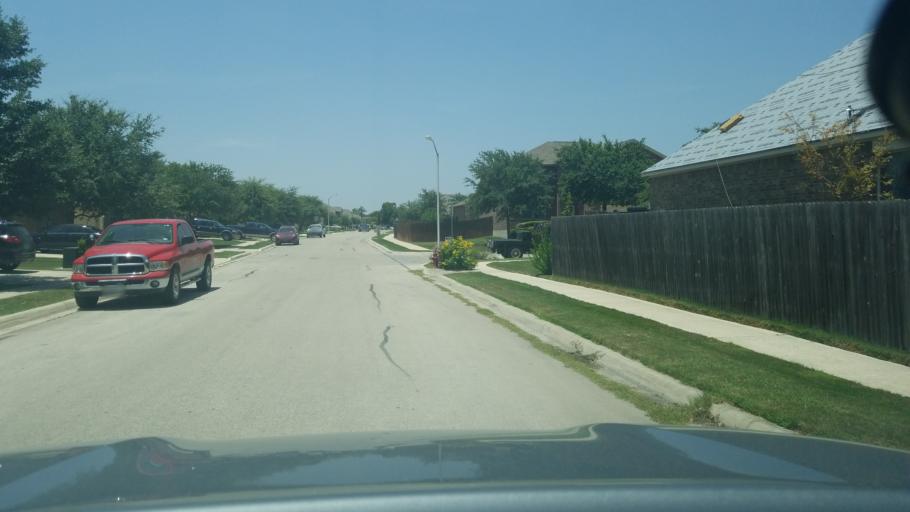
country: US
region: Texas
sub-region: Guadalupe County
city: Cibolo
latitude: 29.5767
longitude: -98.2305
